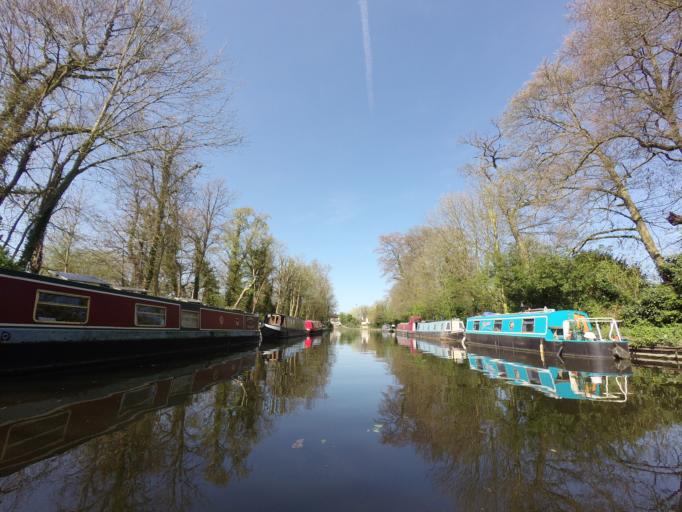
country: GB
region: England
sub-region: Greater London
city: Uxbridge
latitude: 51.5273
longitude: -0.4860
